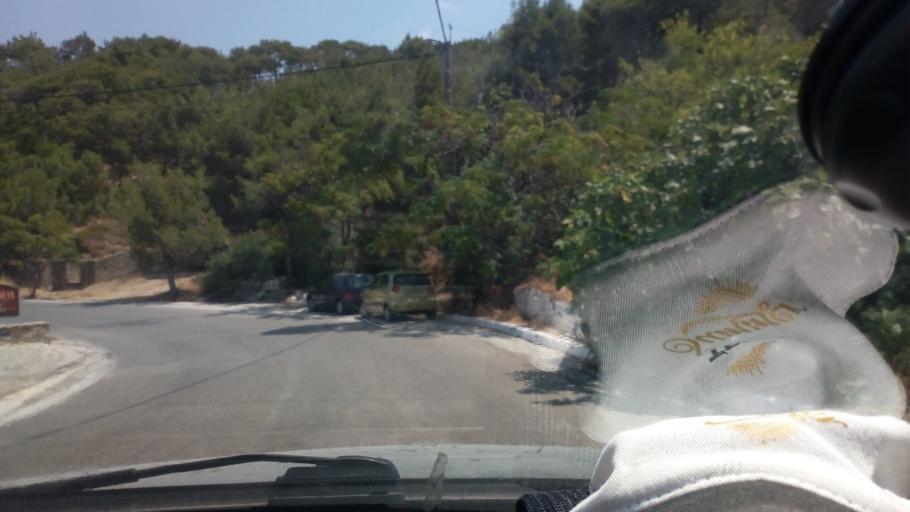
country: GR
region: North Aegean
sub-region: Nomos Samou
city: Agios Kirykos
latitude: 37.6304
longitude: 26.1034
